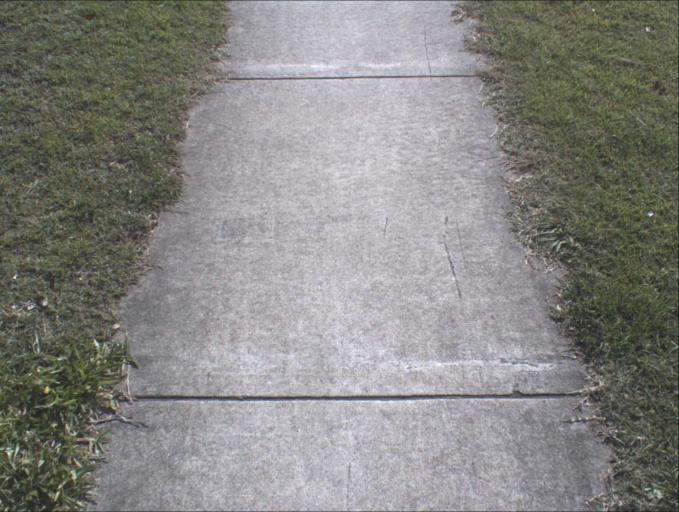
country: AU
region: Queensland
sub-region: Logan
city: Logan Reserve
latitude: -27.6950
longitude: 153.0793
